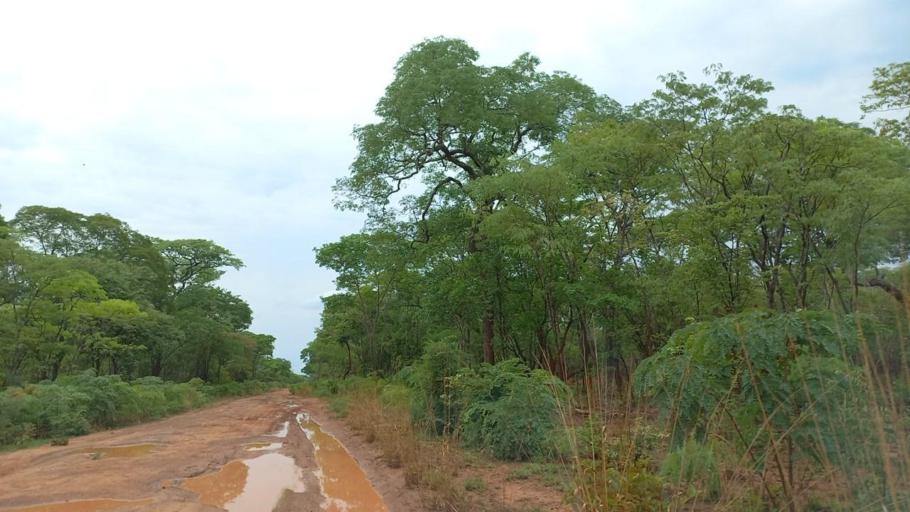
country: ZM
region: North-Western
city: Kalengwa
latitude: -13.6003
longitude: 24.9742
